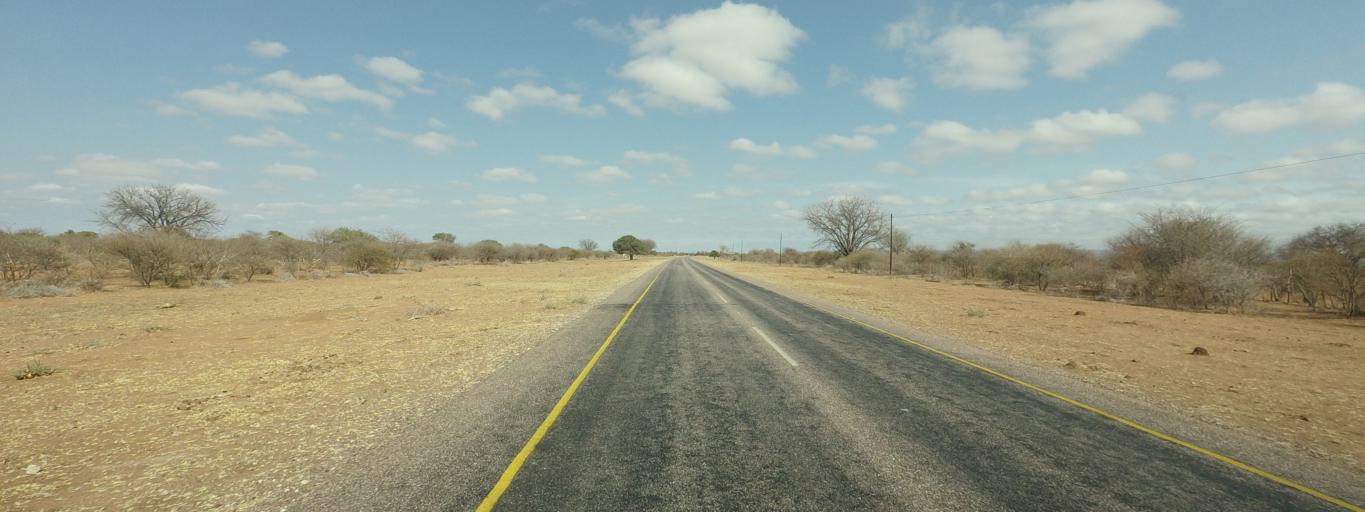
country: BW
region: Central
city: Ratholo
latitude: -22.8103
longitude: 27.5350
